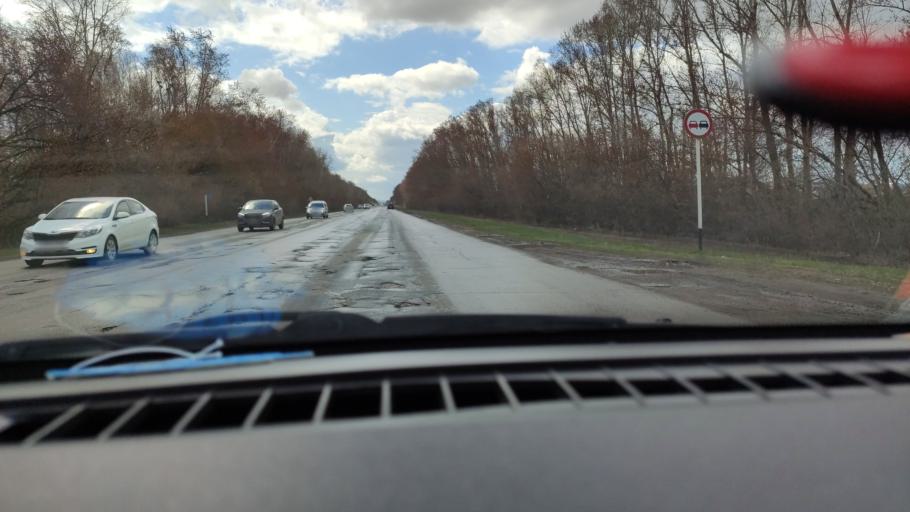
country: RU
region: Samara
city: Tol'yatti
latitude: 53.6263
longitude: 49.4161
